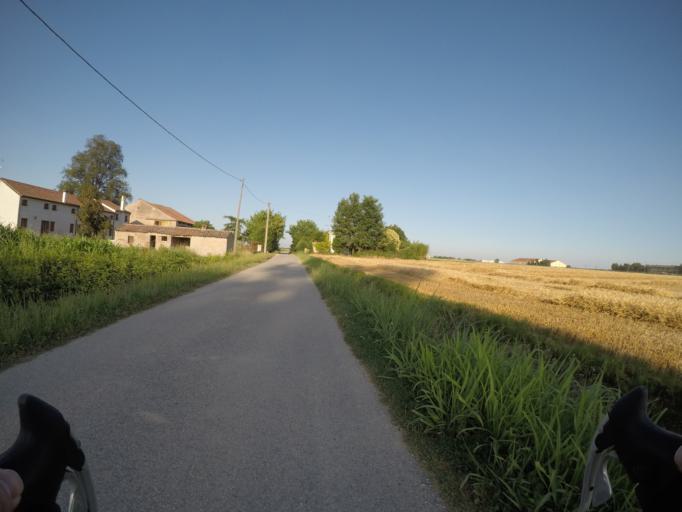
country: IT
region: Veneto
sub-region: Provincia di Rovigo
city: Fratta Polesine
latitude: 45.0264
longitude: 11.6648
